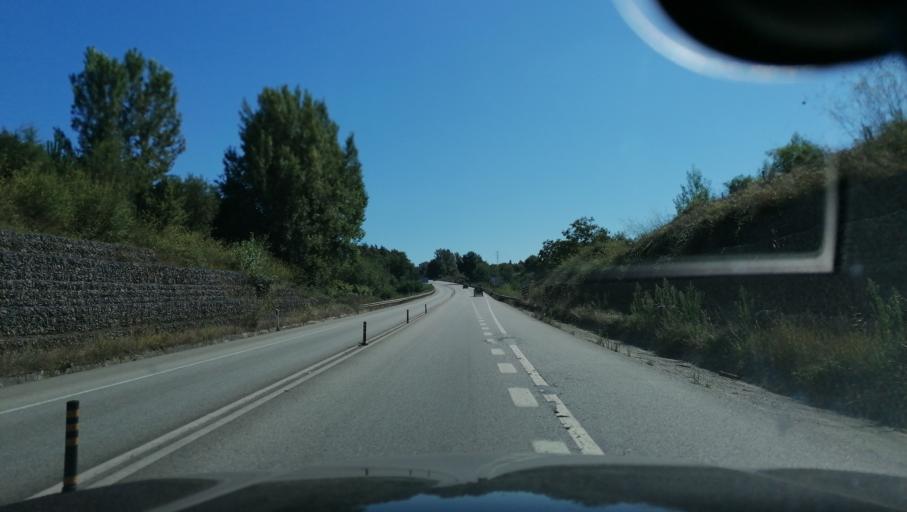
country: PT
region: Aveiro
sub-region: Oliveira de Azemeis
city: Oliveira de Azemeis
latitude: 40.8176
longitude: -8.4734
